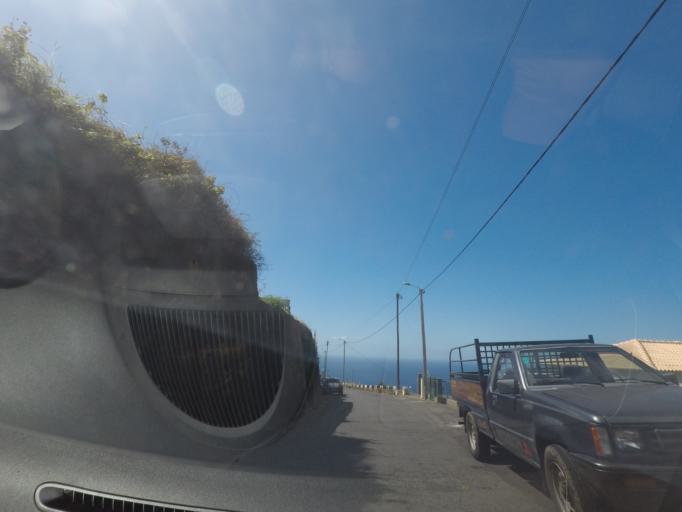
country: PT
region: Madeira
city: Ponta do Sol
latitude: 32.6928
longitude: -17.0877
